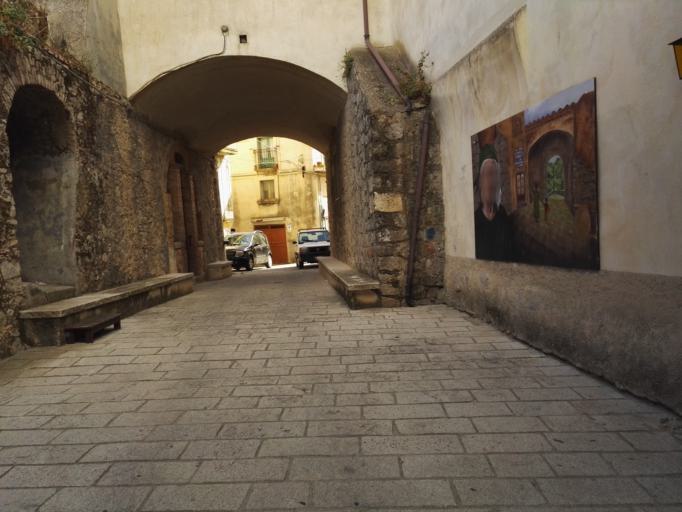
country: IT
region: Calabria
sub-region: Provincia di Reggio Calabria
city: Riace
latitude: 38.4187
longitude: 16.4827
